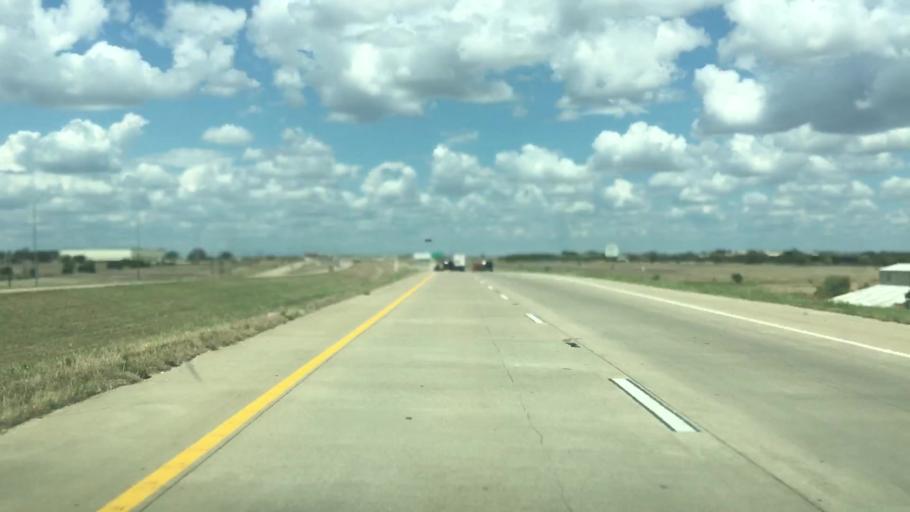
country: US
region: Texas
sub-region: Williamson County
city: Hutto
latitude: 30.5768
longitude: -97.5849
